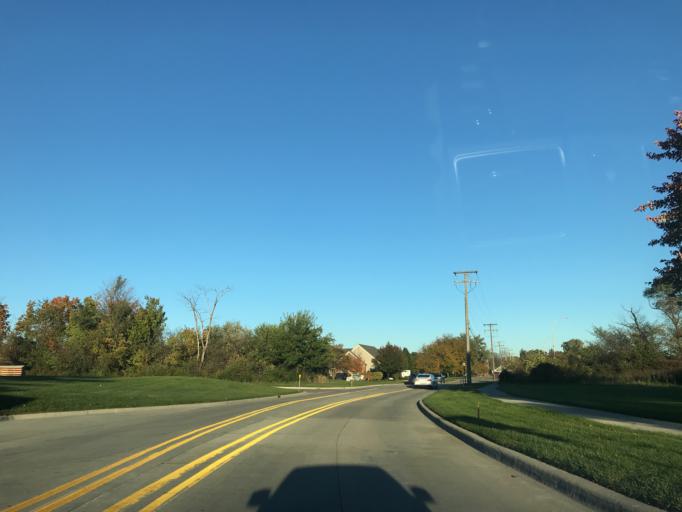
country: US
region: Michigan
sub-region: Oakland County
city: Clawson
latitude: 42.5675
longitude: -83.1538
